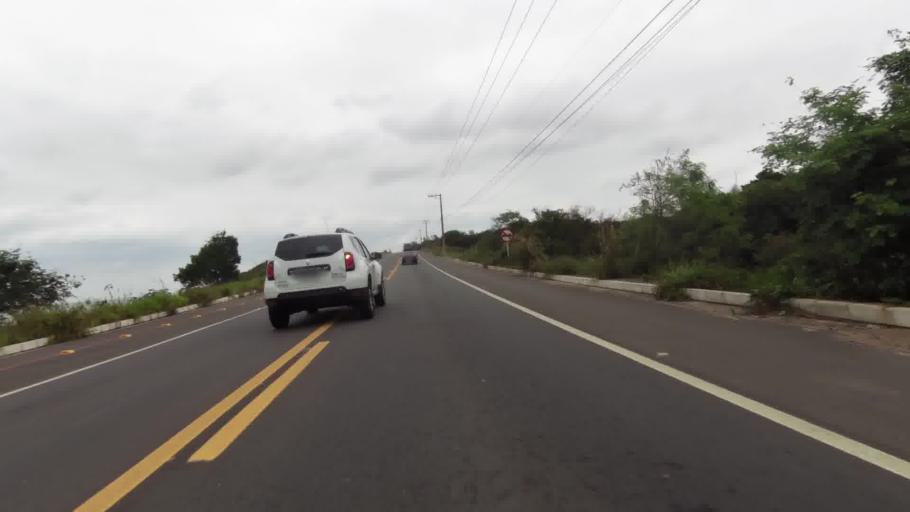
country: BR
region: Espirito Santo
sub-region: Piuma
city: Piuma
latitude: -20.8087
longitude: -40.6114
